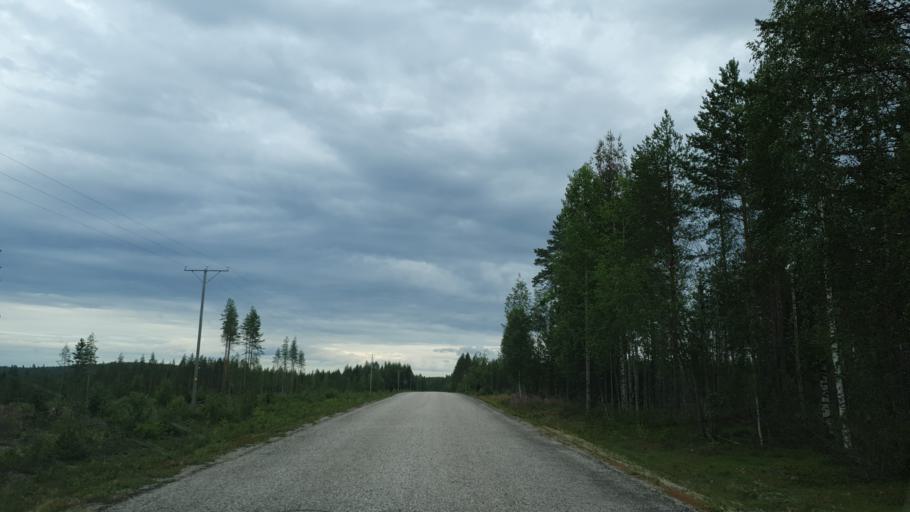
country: FI
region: Kainuu
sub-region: Kehys-Kainuu
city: Kuhmo
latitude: 64.3432
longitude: 29.2944
